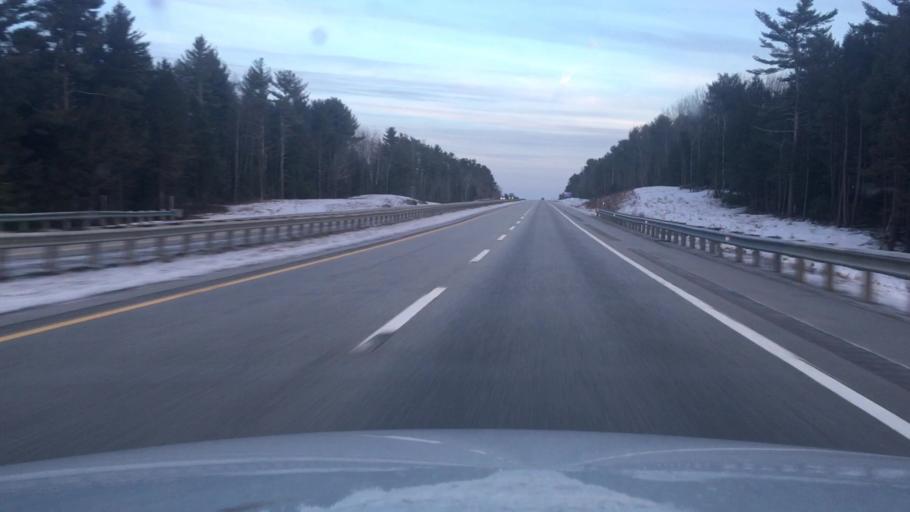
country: US
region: Maine
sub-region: Sagadahoc County
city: Richmond
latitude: 44.1560
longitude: -69.8990
